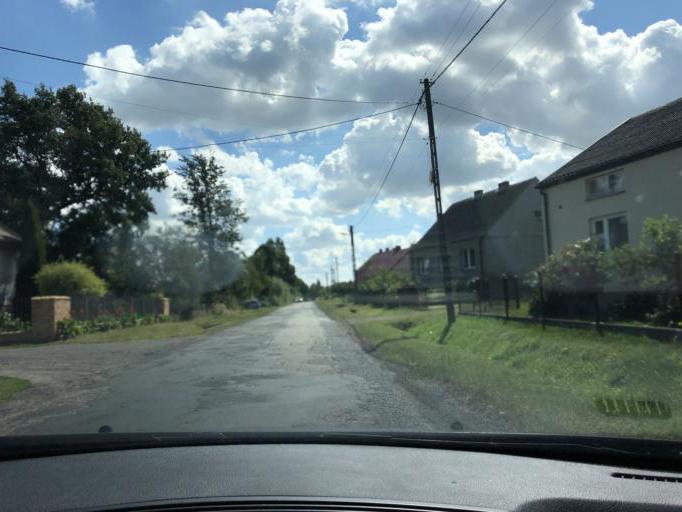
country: PL
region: Lodz Voivodeship
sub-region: Powiat wieruszowski
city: Czastary
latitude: 51.2357
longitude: 18.3450
